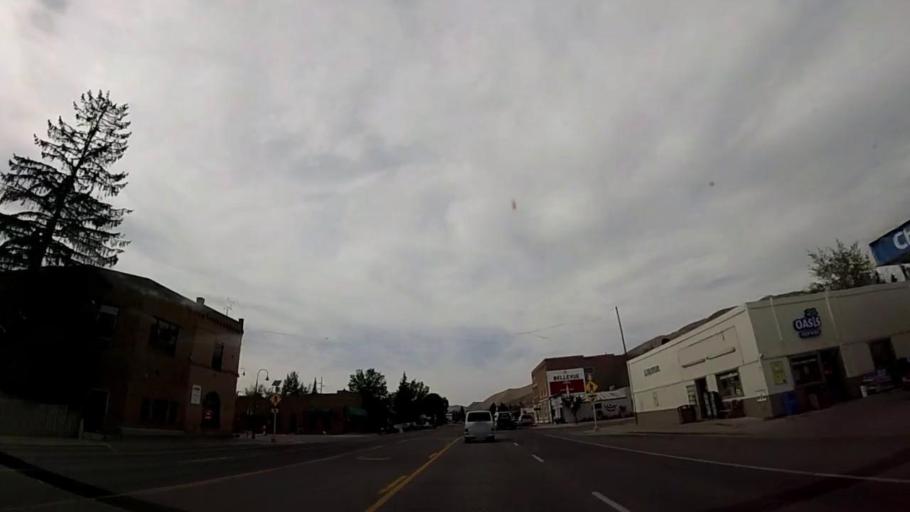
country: US
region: Idaho
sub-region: Blaine County
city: Bellevue
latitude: 43.4633
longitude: -114.2604
